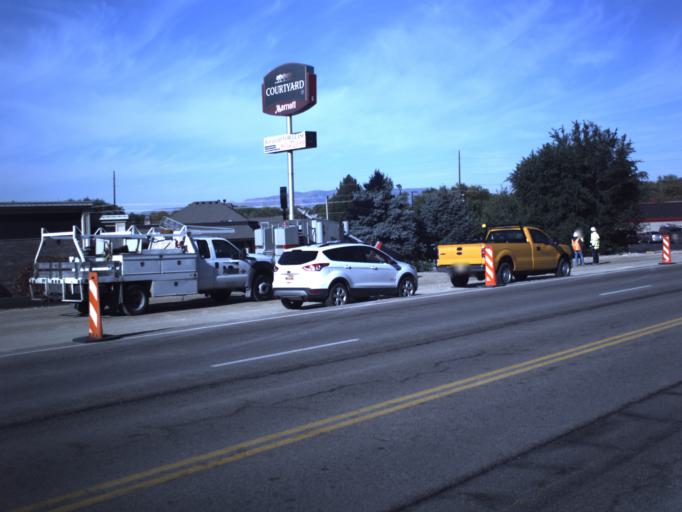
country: US
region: Utah
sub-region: Utah County
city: Provo
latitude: 40.2563
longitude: -111.6600
